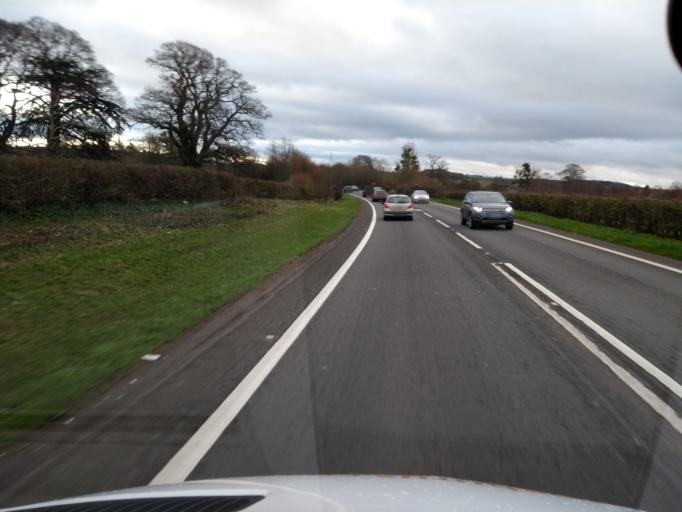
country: GB
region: England
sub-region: Somerset
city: Ilminster
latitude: 50.9387
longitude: -2.9491
